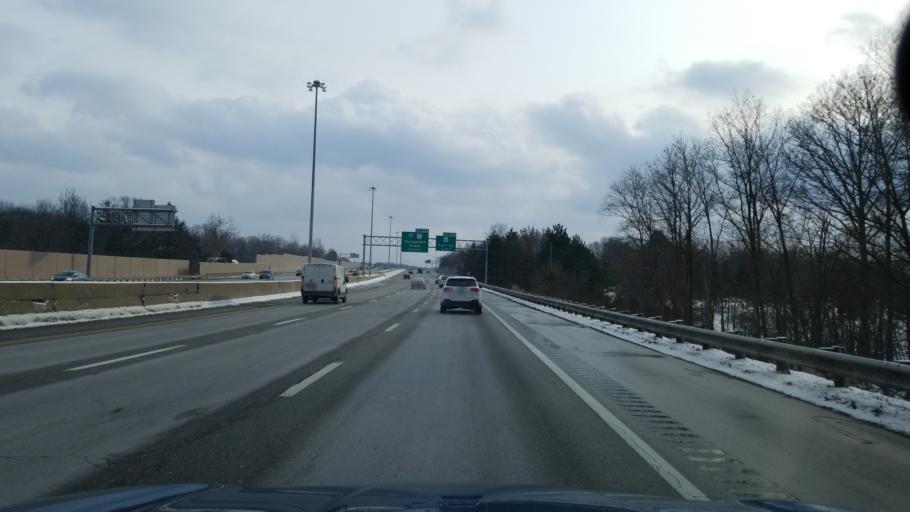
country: US
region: Ohio
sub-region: Cuyahoga County
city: Middleburg Heights
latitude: 41.3638
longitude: -81.8215
